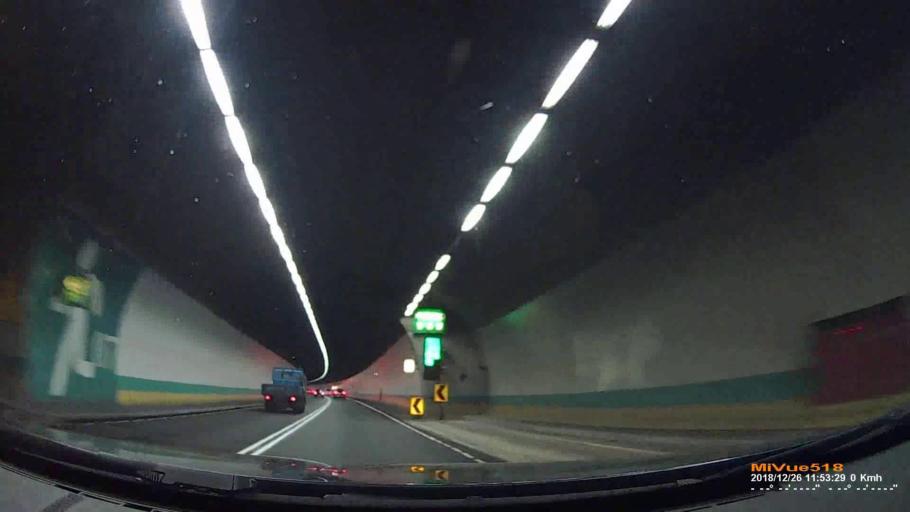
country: TW
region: Taiwan
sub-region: Keelung
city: Keelung
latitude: 24.9580
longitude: 121.6929
